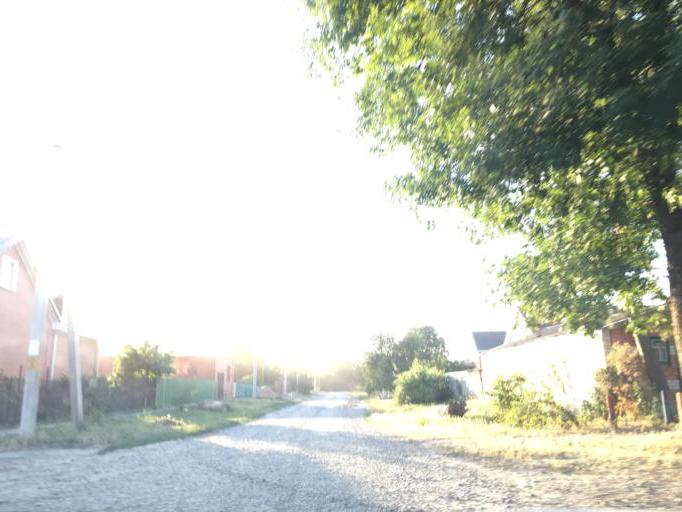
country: RU
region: Krasnodarskiy
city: Kushchevskaya
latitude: 46.5646
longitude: 39.6508
